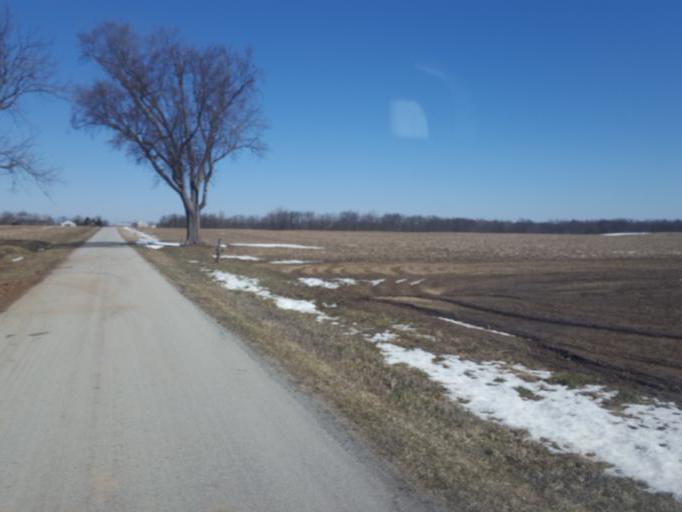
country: US
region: Ohio
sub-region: Marion County
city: Marion
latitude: 40.7455
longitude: -83.1450
